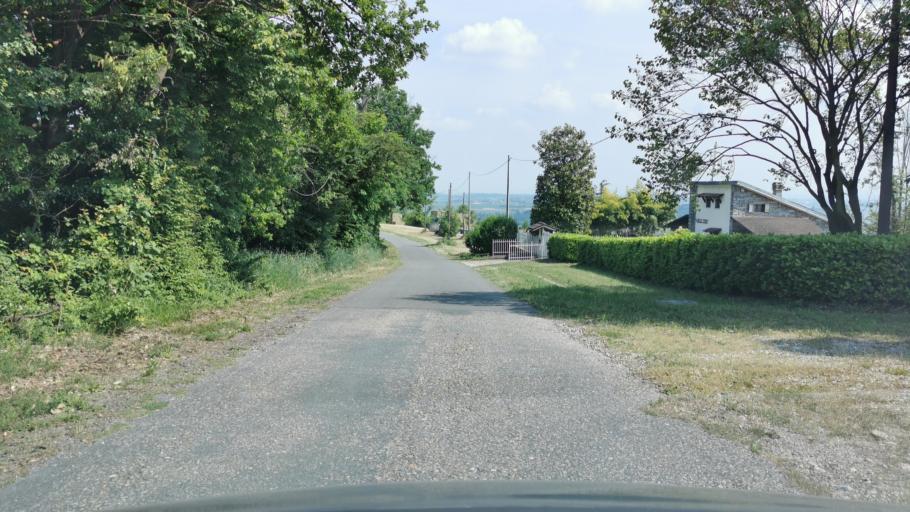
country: IT
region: Piedmont
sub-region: Provincia di Asti
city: Grazzano Badoglio
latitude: 45.0542
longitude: 8.3155
